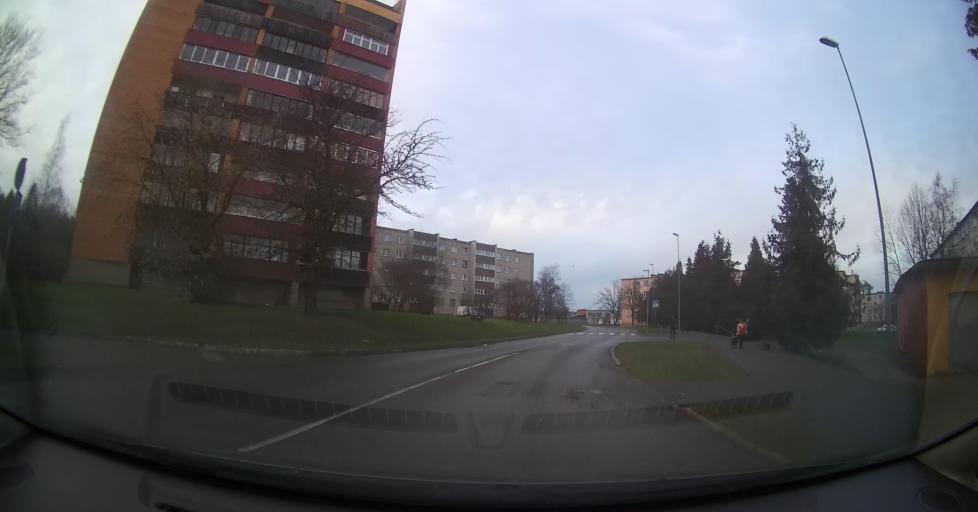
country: EE
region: Ida-Virumaa
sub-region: Johvi vald
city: Johvi
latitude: 59.3496
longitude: 27.4146
